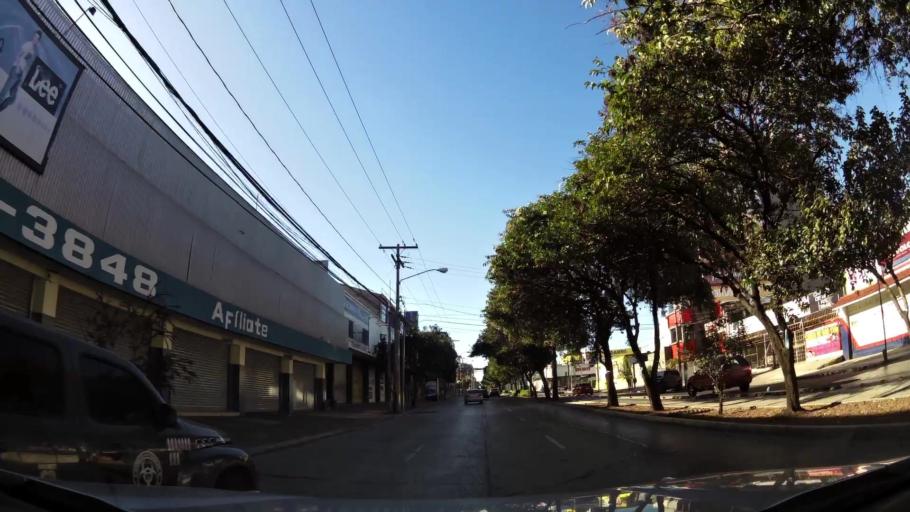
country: GT
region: Guatemala
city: Guatemala City
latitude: 14.6129
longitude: -90.5183
